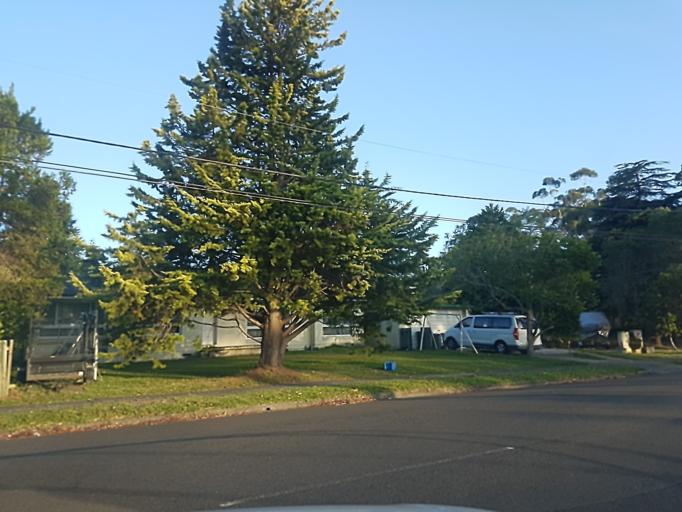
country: AU
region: New South Wales
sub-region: Warringah
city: Davidson
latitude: -33.7414
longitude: 151.2083
